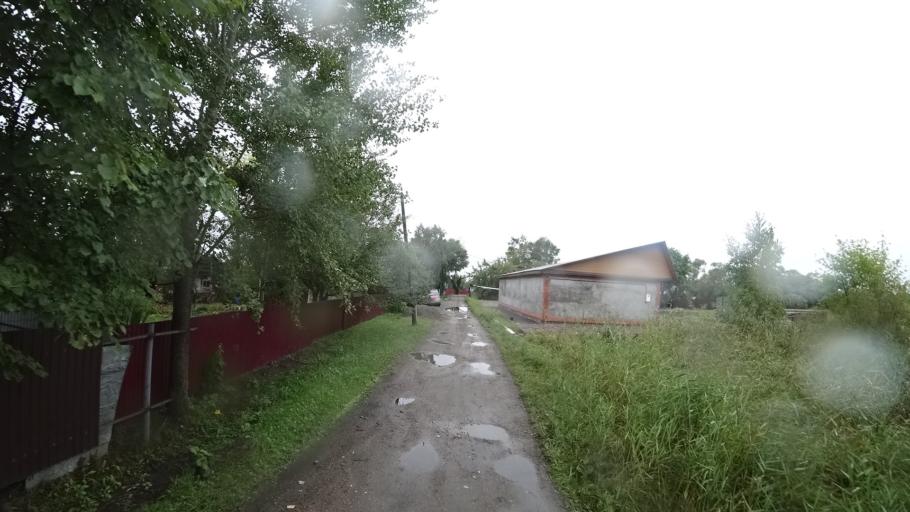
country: RU
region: Primorskiy
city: Monastyrishche
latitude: 44.1967
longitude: 132.4235
